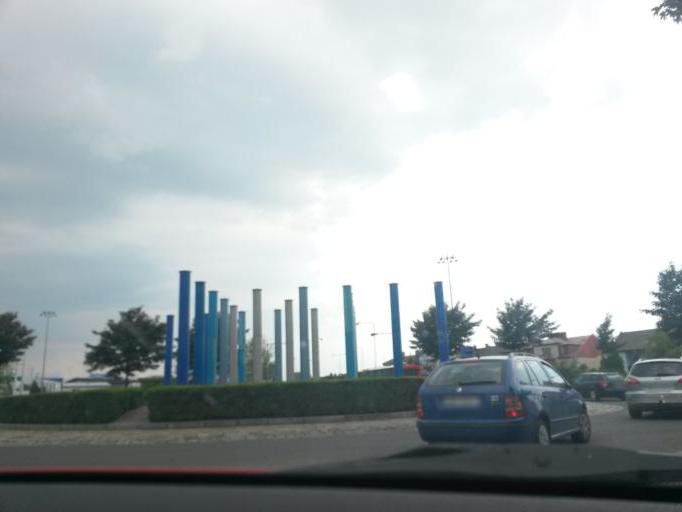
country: CZ
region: Olomoucky
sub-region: Okres Olomouc
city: Olomouc
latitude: 49.5900
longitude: 17.2779
